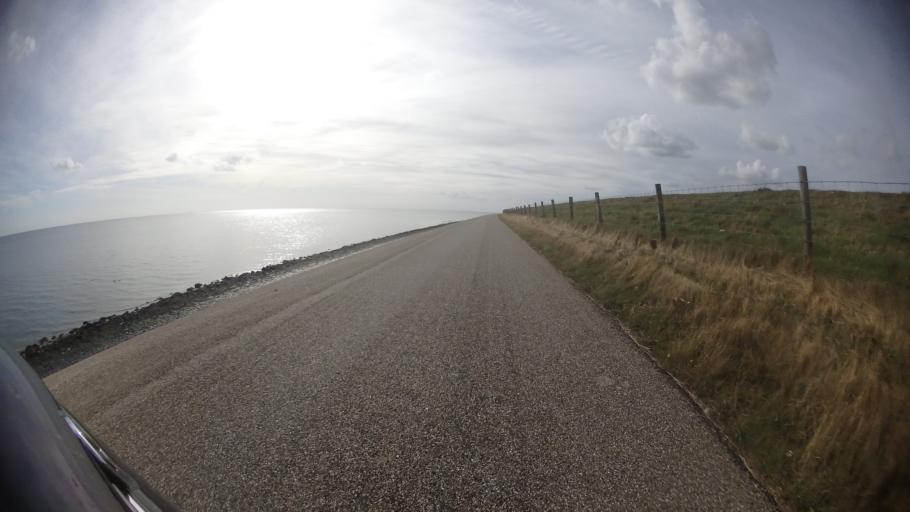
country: NL
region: North Holland
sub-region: Gemeente Texel
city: Den Burg
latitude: 53.0880
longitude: 4.9002
